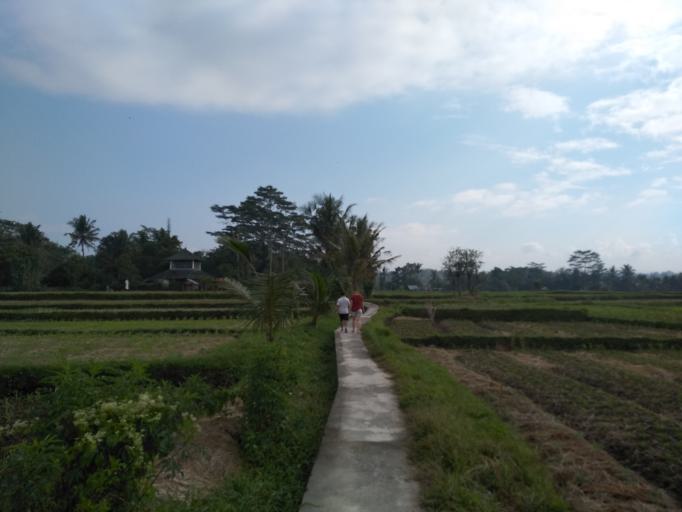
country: ID
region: Bali
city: Banjar Pande
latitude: -8.4936
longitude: 115.2477
